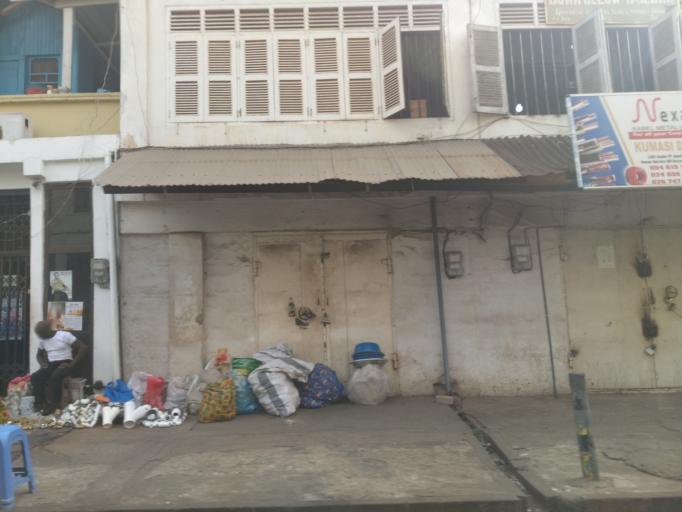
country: GH
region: Ashanti
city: Kumasi
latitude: 6.6939
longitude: -1.6226
